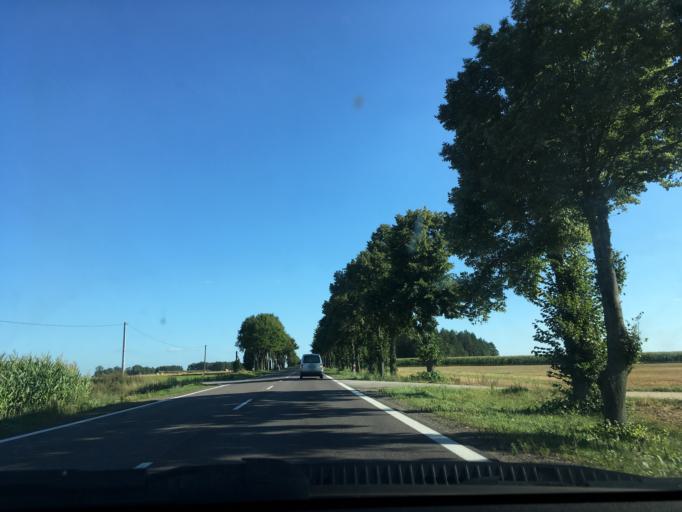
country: PL
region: Podlasie
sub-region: Powiat sokolski
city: Janow
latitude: 53.4327
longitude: 23.1013
